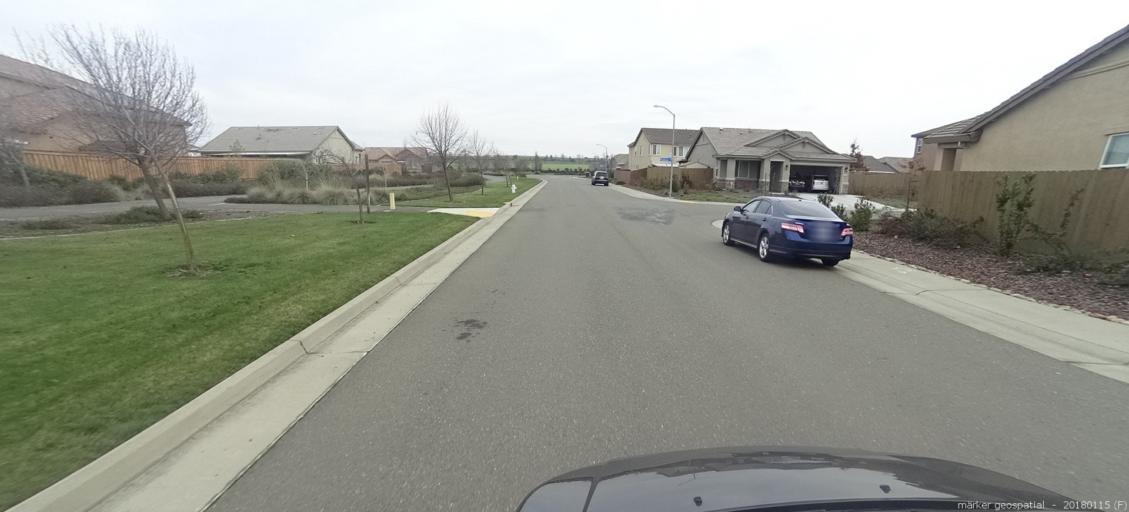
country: US
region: California
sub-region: Sacramento County
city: Rancho Cordova
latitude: 38.5756
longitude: -121.2711
